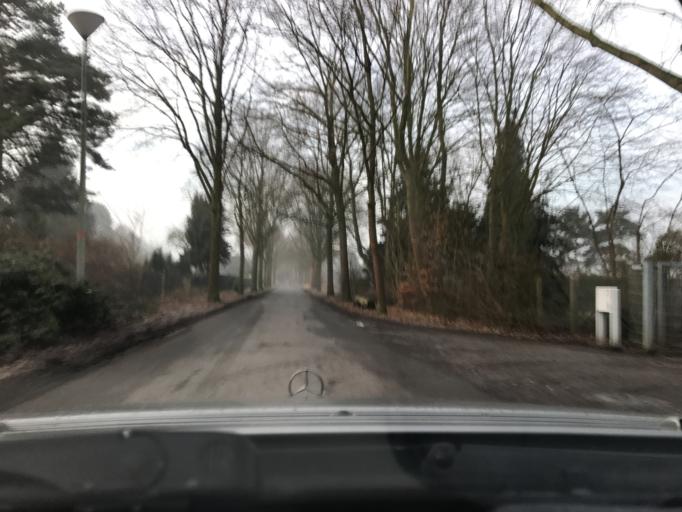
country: DE
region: North Rhine-Westphalia
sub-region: Regierungsbezirk Dusseldorf
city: Krefeld
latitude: 51.3560
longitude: 6.5472
